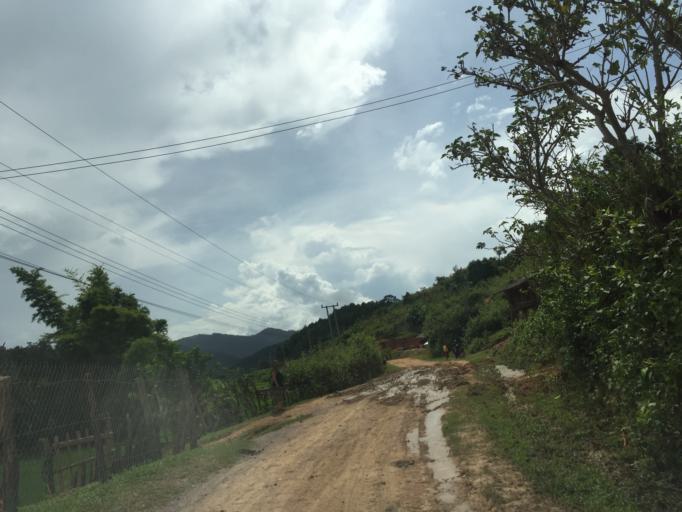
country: LA
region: Xiangkhoang
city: Muang Phonsavan
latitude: 19.3400
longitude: 103.5352
